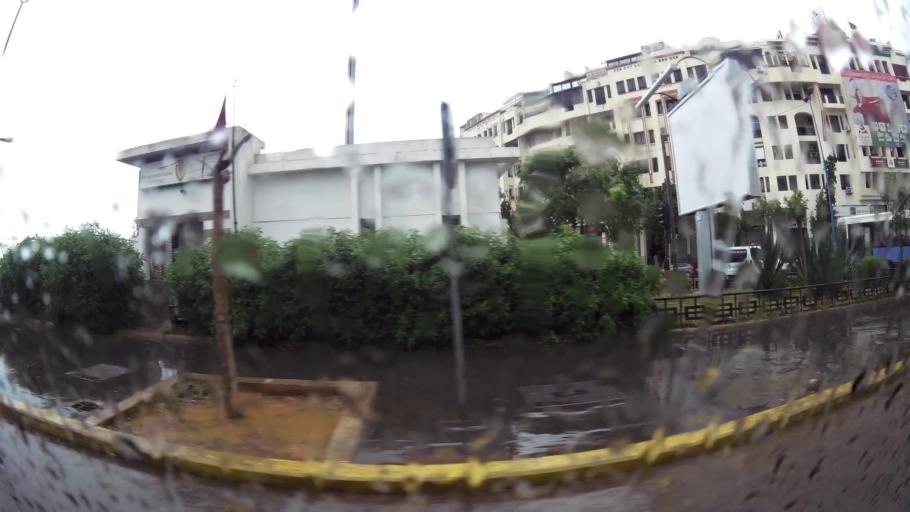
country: MA
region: Grand Casablanca
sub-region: Casablanca
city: Casablanca
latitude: 33.5696
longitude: -7.6286
